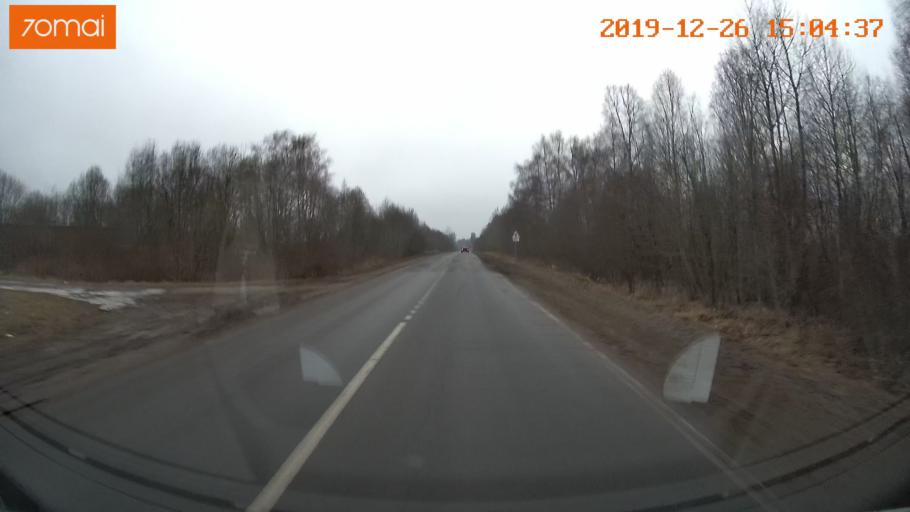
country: RU
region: Jaroslavl
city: Rybinsk
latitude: 58.1978
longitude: 38.8598
